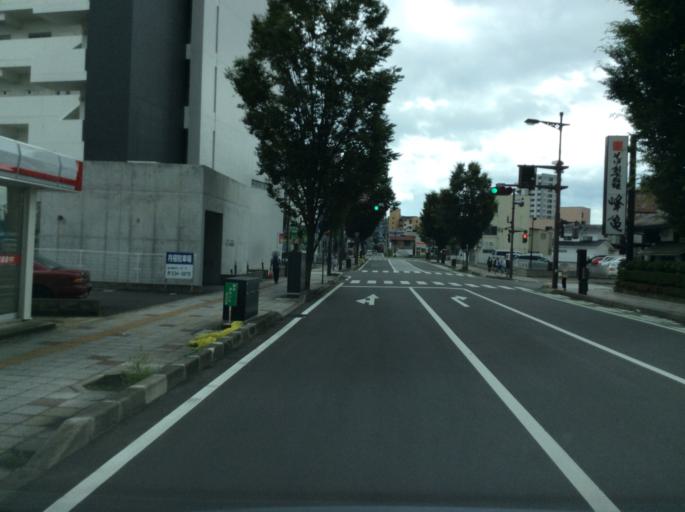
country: JP
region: Fukushima
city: Fukushima-shi
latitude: 37.7607
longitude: 140.4604
